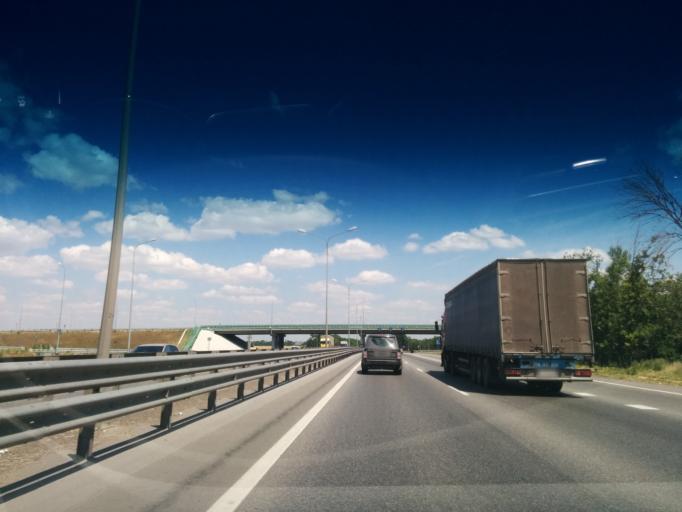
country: RU
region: Rostov
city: Grushevskaya
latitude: 47.3763
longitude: 39.9059
